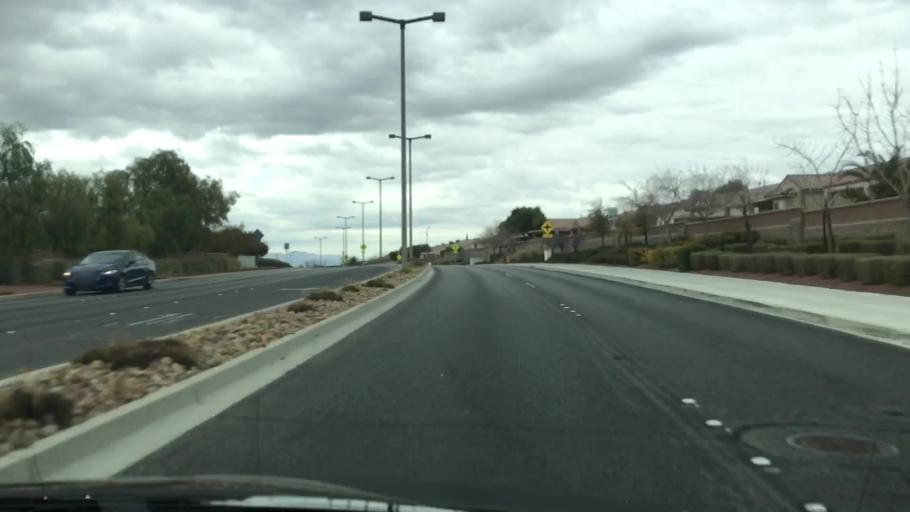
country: US
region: Nevada
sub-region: Clark County
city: Whitney
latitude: 35.9513
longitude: -115.1146
